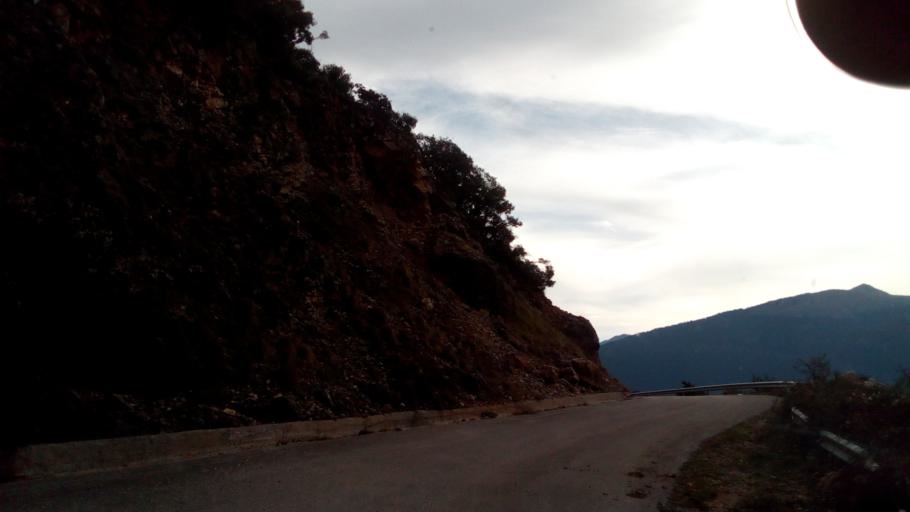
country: GR
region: West Greece
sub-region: Nomos Aitolias kai Akarnanias
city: Thermo
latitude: 38.6809
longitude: 21.8762
